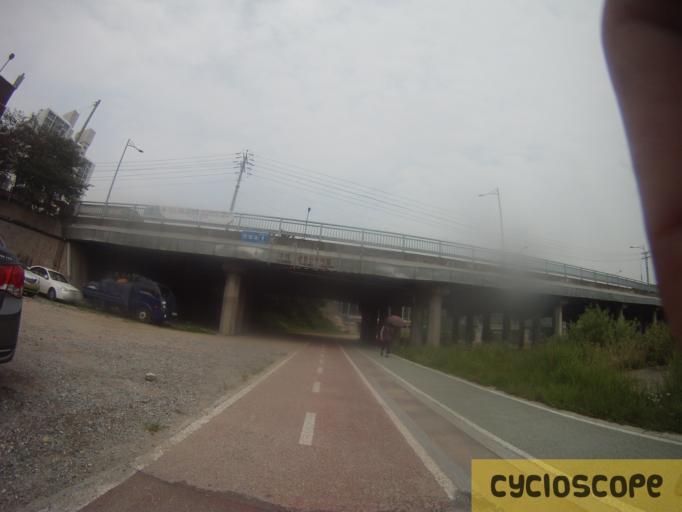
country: KR
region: Gyeonggi-do
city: Anyang-si
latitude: 37.4102
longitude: 126.9159
